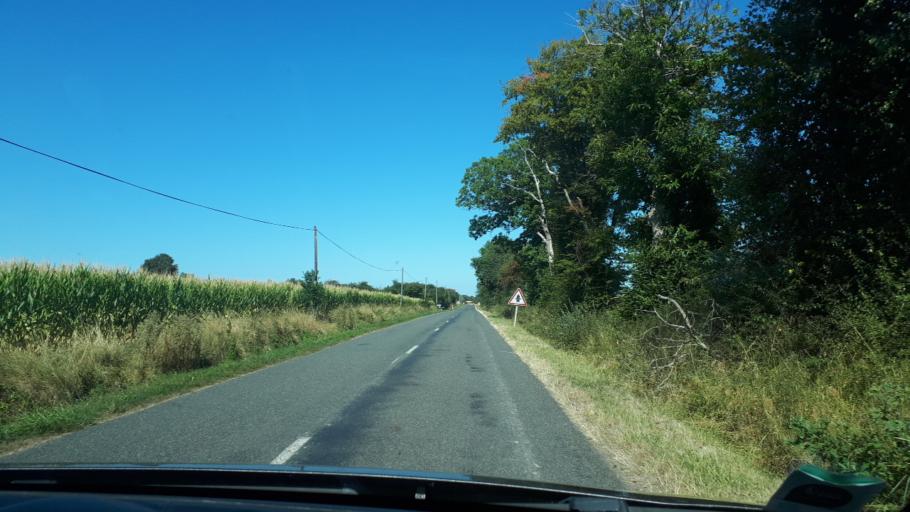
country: FR
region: Centre
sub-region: Departement du Loiret
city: Briare
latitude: 47.5905
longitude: 2.7257
